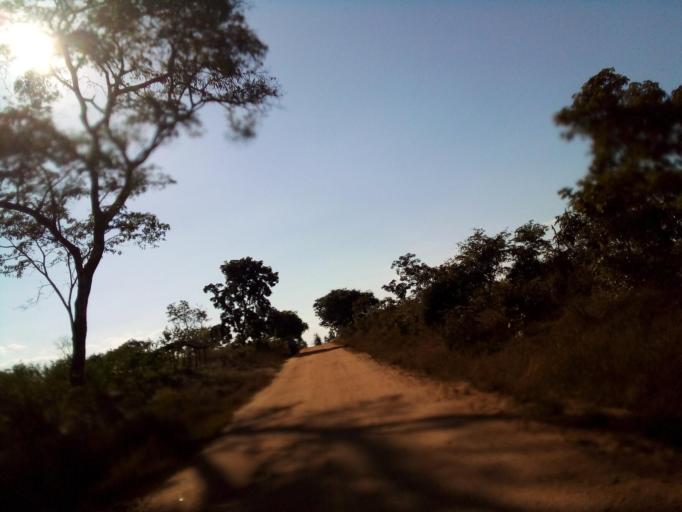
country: MZ
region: Zambezia
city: Quelimane
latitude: -17.5015
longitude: 36.5802
